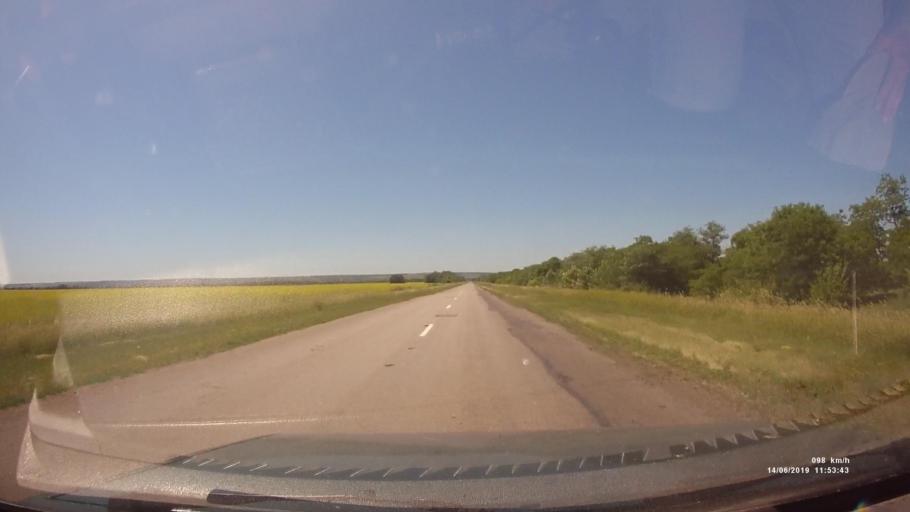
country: RU
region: Rostov
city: Kazanskaya
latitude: 49.8252
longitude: 41.2072
